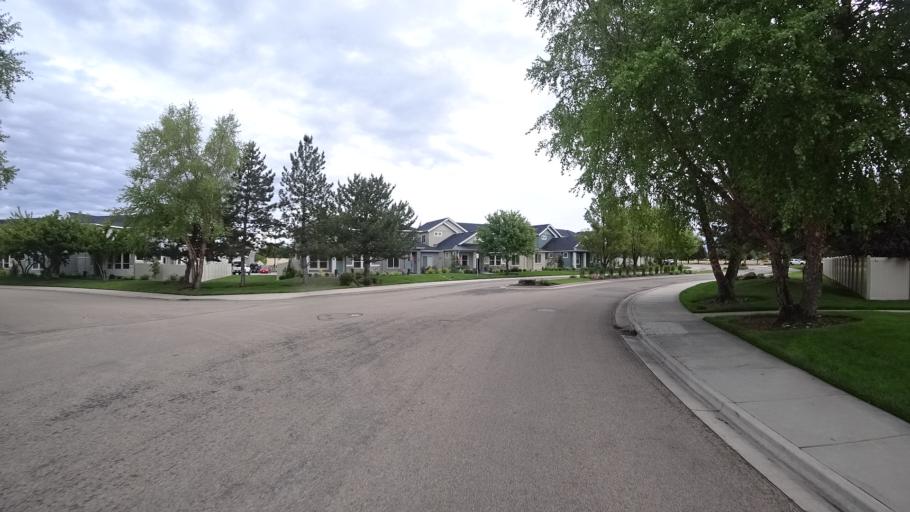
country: US
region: Idaho
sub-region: Ada County
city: Star
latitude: 43.6909
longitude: -116.5052
